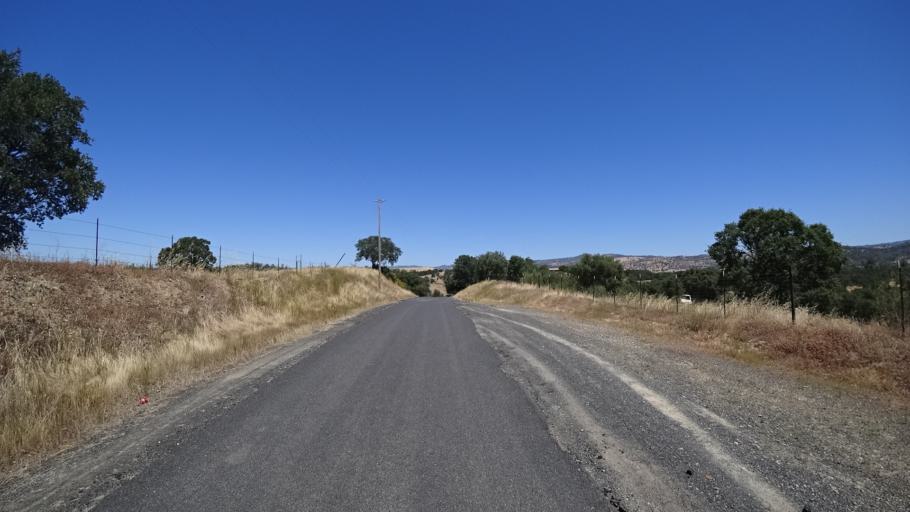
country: US
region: California
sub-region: Calaveras County
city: Copperopolis
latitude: 37.9830
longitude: -120.6914
